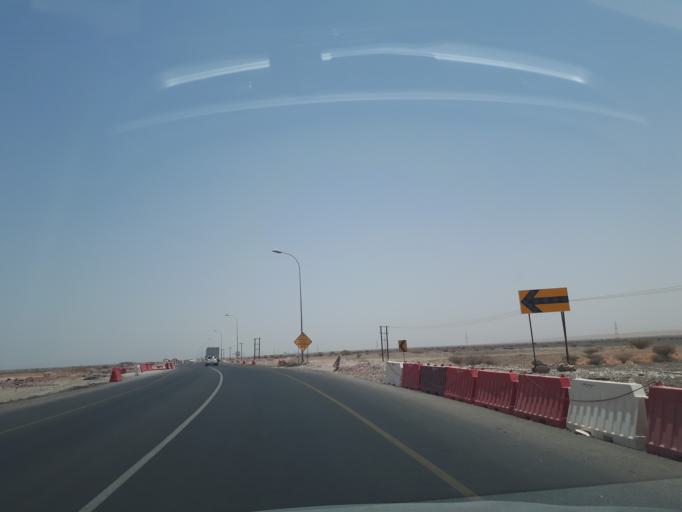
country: OM
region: Ash Sharqiyah
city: Badiyah
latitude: 22.4301
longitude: 59.0348
